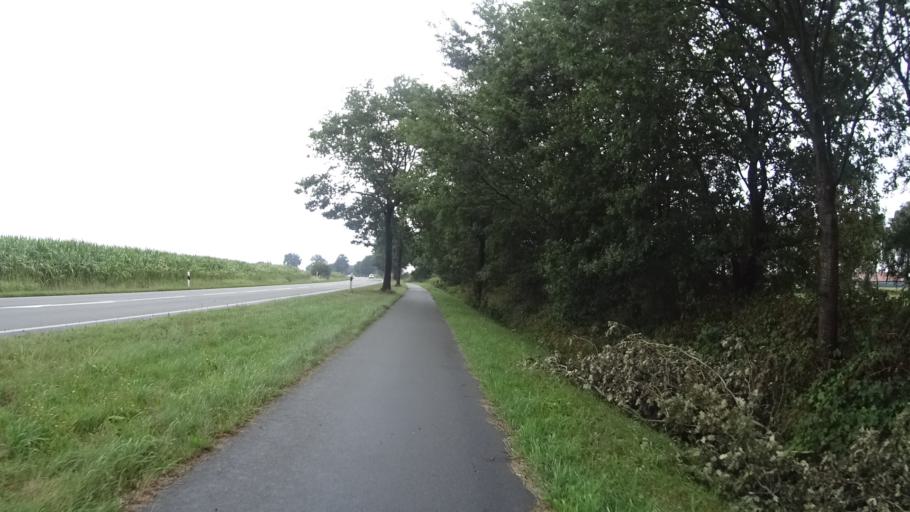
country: DE
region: Lower Saxony
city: Brinkum
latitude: 53.2720
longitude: 7.5592
